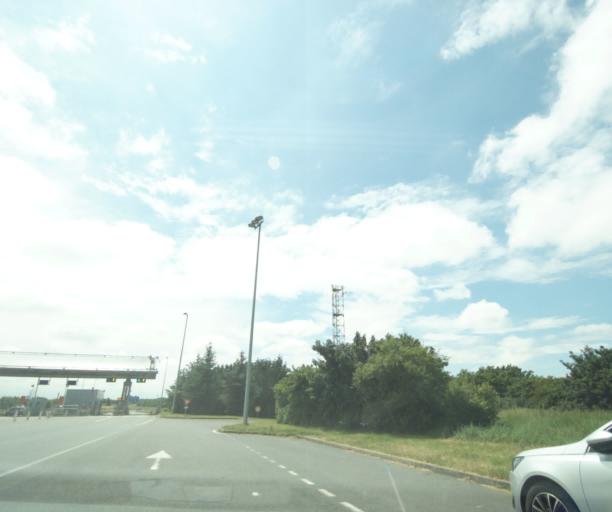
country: FR
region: Poitou-Charentes
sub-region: Departement des Deux-Sevres
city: Echire
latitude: 46.4201
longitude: -0.3971
